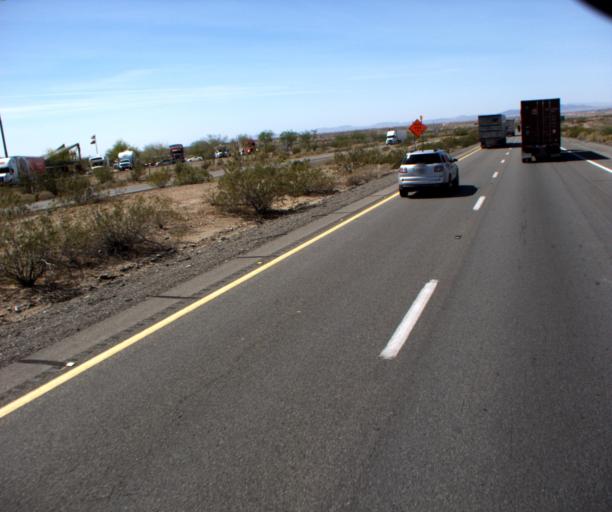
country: US
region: Arizona
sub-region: La Paz County
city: Ehrenberg
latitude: 33.6194
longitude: -114.4519
